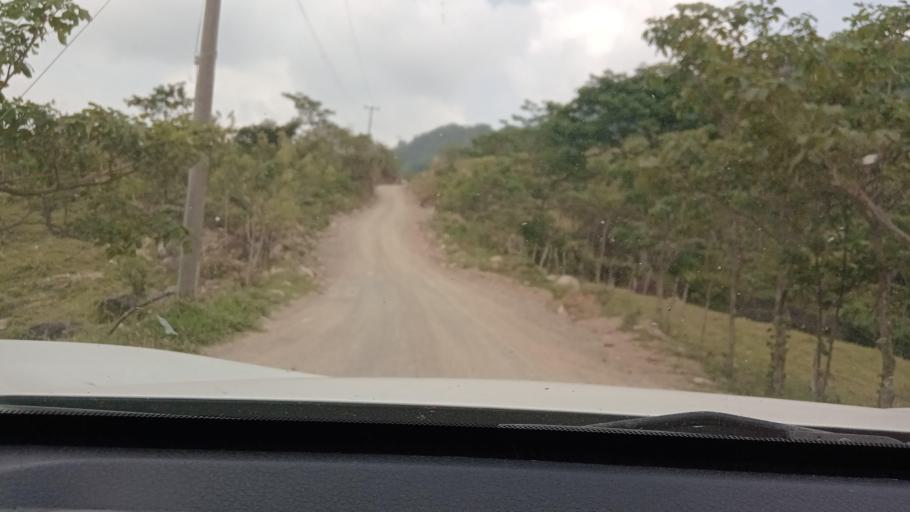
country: MX
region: Tabasco
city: Chontalpa
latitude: 17.4945
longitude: -93.6550
